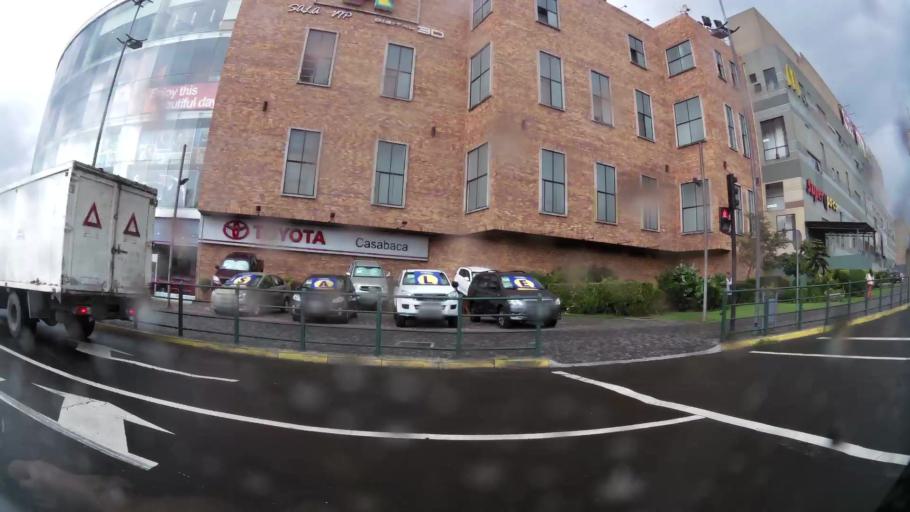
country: EC
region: Pichincha
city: Quito
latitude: -0.1027
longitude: -78.4909
